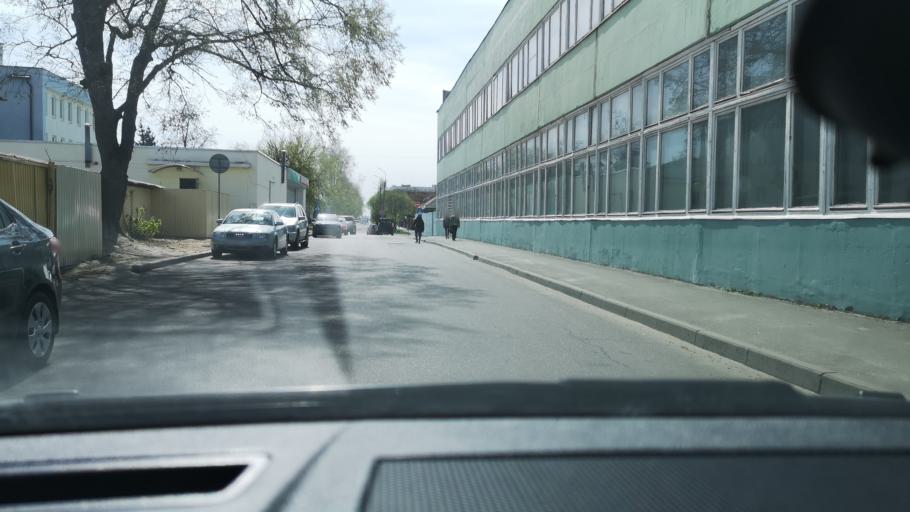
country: BY
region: Gomel
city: Gomel
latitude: 52.4208
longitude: 31.0089
